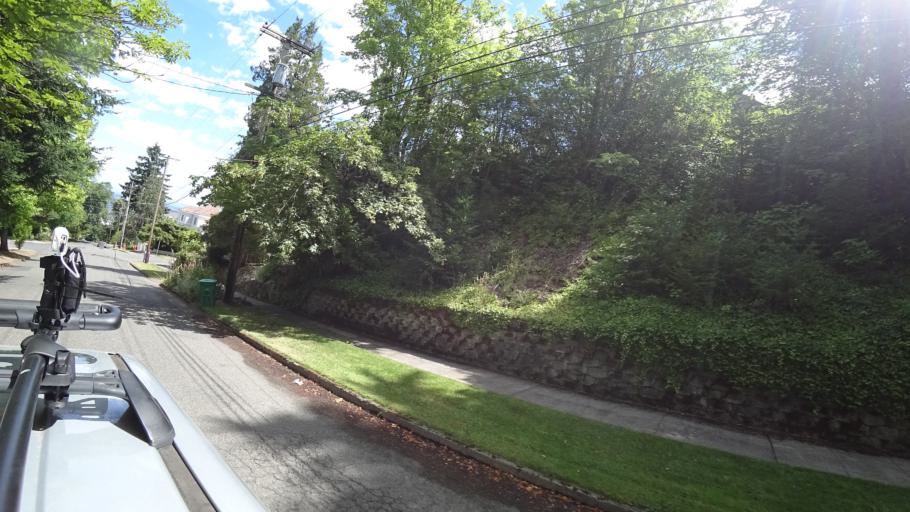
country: US
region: Oregon
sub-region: Multnomah County
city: Portland
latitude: 45.5099
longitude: -122.6946
